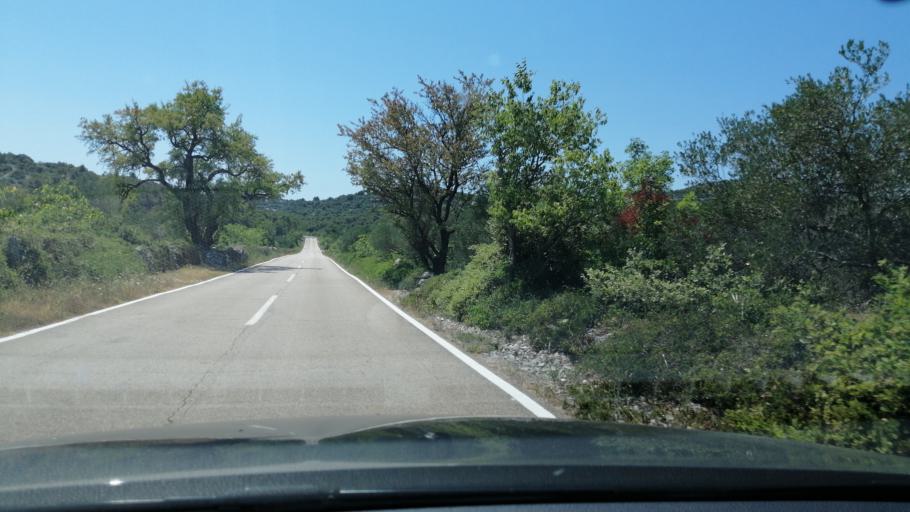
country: HR
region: Sibensko-Kniniska
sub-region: Grad Sibenik
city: Pirovac
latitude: 43.8492
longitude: 15.6872
